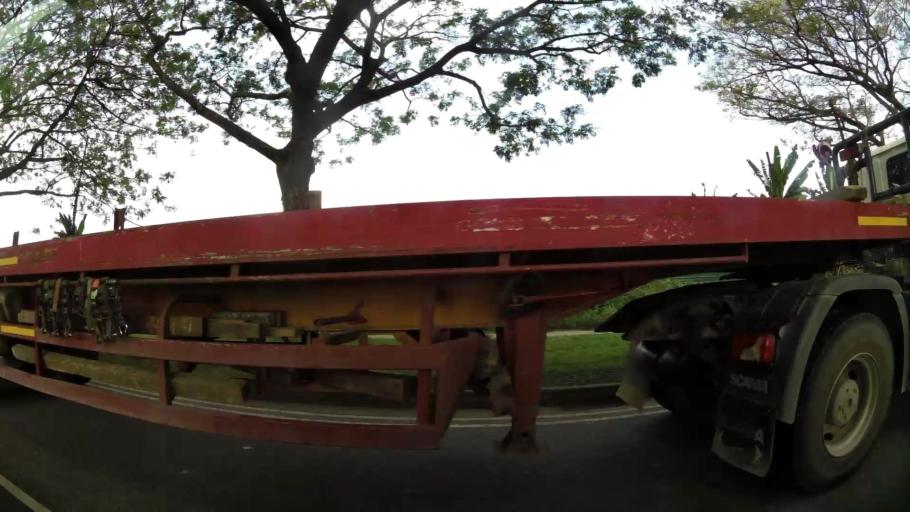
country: MY
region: Johor
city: Johor Bahru
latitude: 1.3226
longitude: 103.6301
